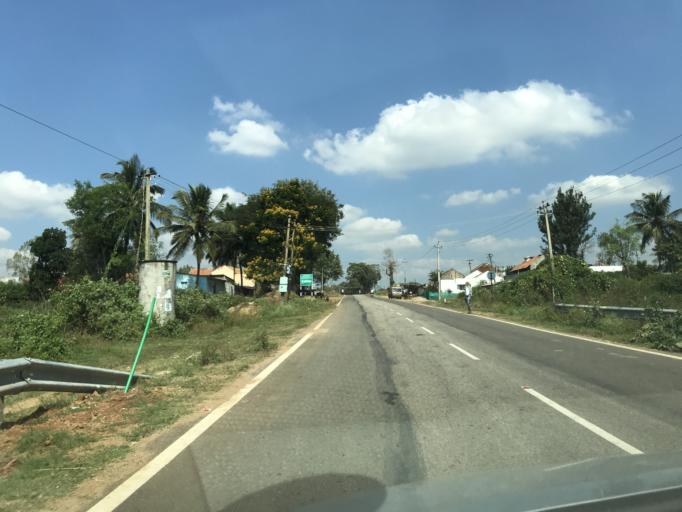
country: IN
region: Karnataka
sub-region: Mysore
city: Heggadadevankote
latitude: 12.1691
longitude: 76.2799
